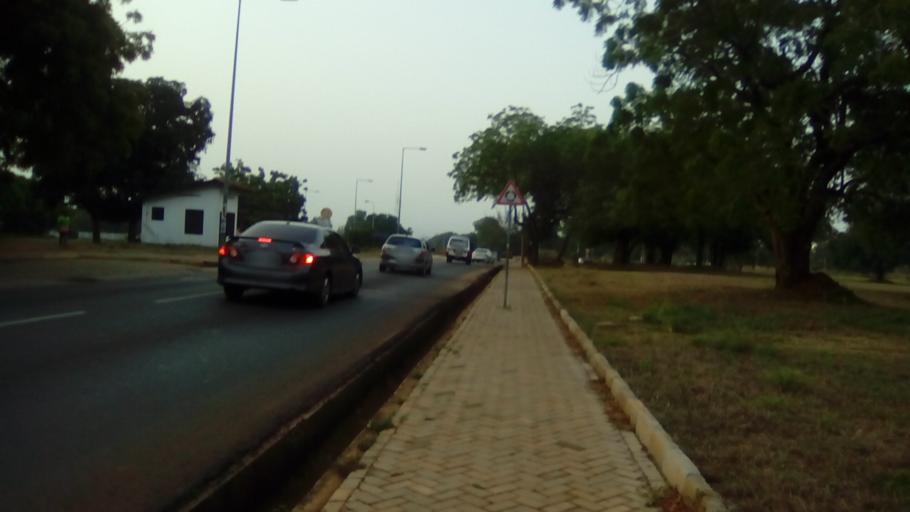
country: GH
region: Greater Accra
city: Medina Estates
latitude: 5.6412
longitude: -0.1840
